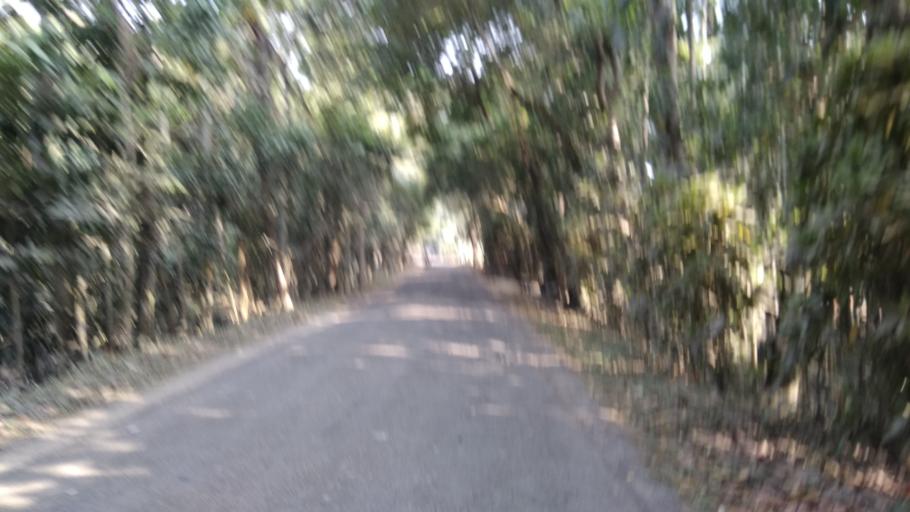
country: BD
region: Barisal
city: Mehendiganj
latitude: 22.9771
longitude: 90.4168
